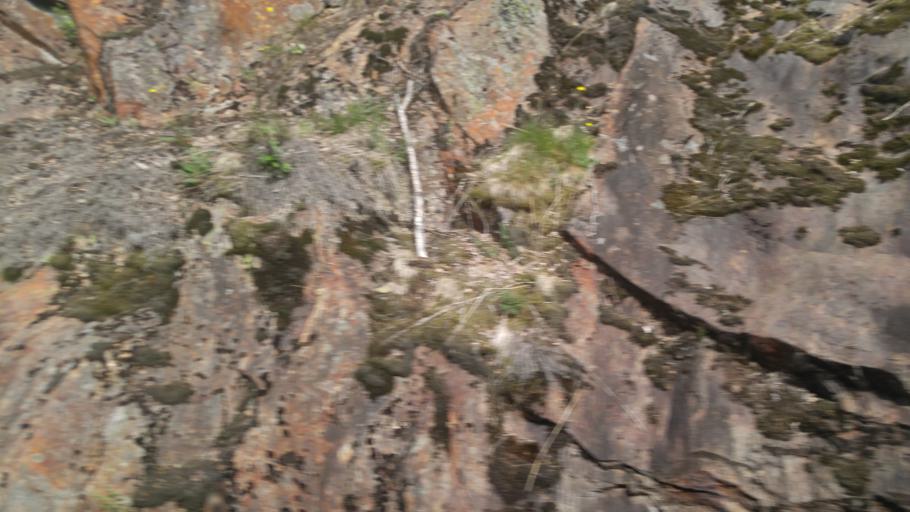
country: NO
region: Sor-Trondelag
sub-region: Midtre Gauldal
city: Storen
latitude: 62.9969
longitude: 10.4791
